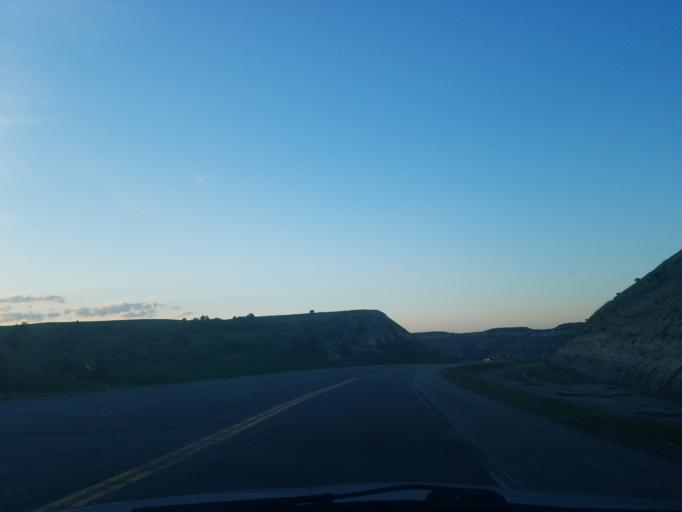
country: US
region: North Dakota
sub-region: McKenzie County
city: Watford City
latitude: 47.5582
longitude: -103.2397
